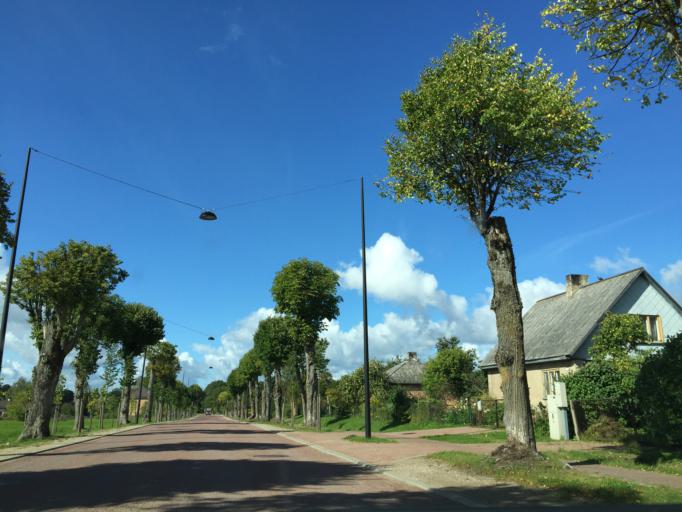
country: LV
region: Kuldigas Rajons
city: Kuldiga
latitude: 56.9710
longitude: 21.9857
